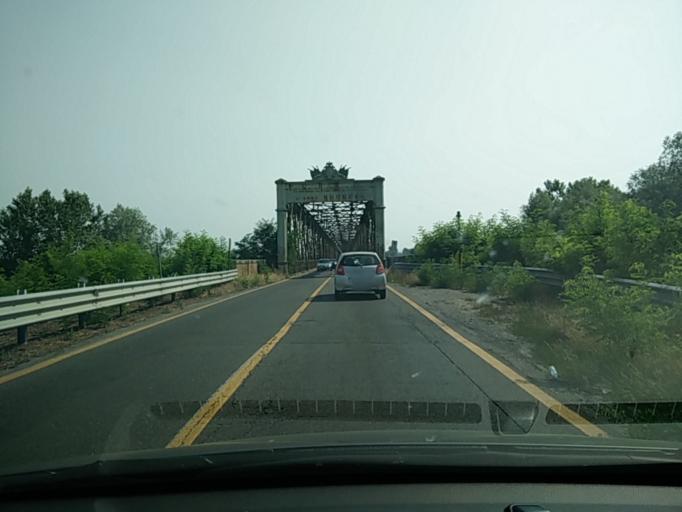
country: IT
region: Lombardy
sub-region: Provincia di Pavia
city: Valle Salimbene
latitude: 45.1453
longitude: 9.2287
